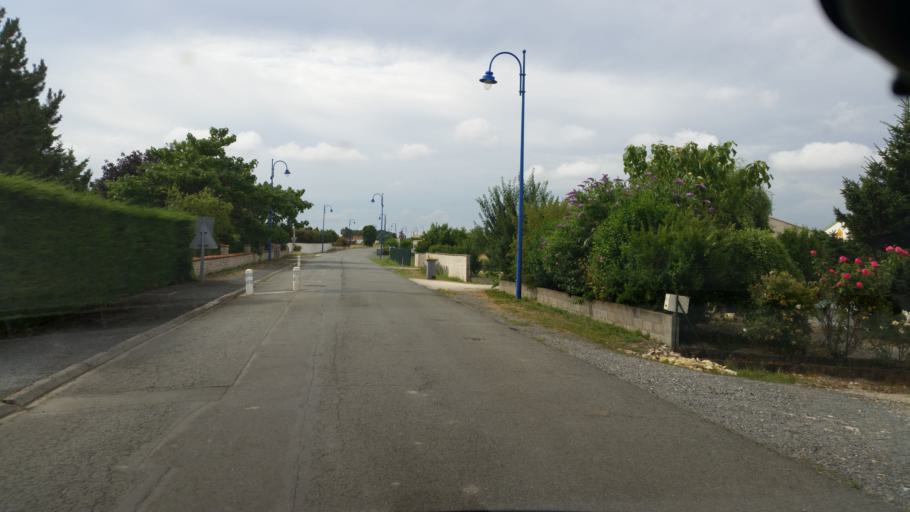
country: FR
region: Poitou-Charentes
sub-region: Departement de la Charente-Maritime
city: Courcon
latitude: 46.1912
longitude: -0.8653
